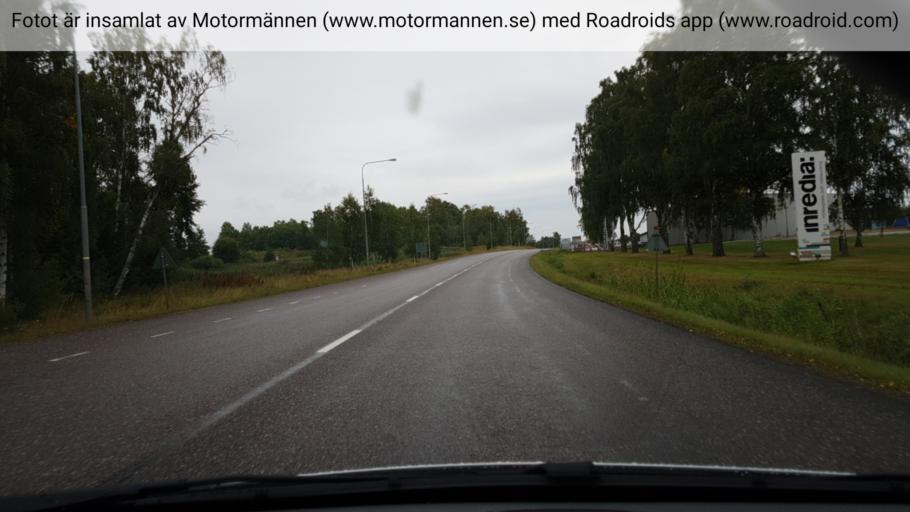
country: SE
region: Vaestra Goetaland
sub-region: Tibro Kommun
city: Tibro
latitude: 58.4312
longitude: 14.1509
